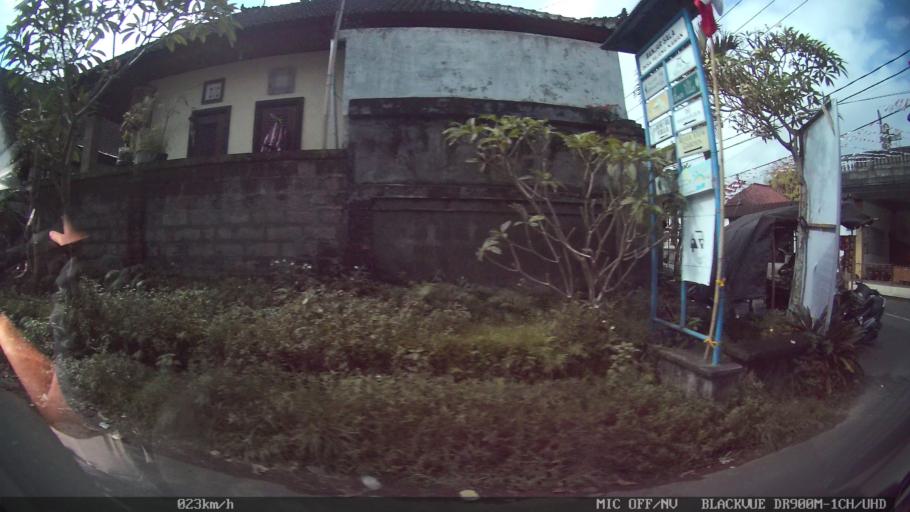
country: ID
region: Bali
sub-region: Kabupaten Gianyar
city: Ubud
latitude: -8.5080
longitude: 115.2824
